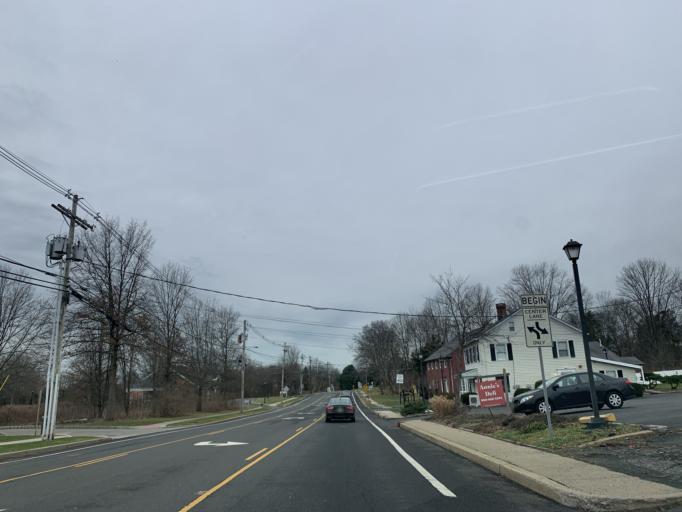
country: US
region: New Jersey
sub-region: Somerset County
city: Bedminster
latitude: 40.6466
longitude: -74.6409
